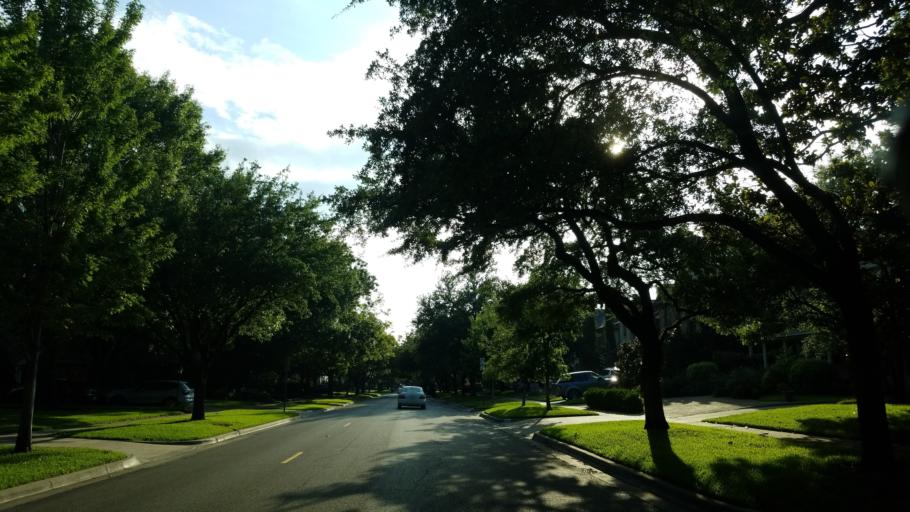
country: US
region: Texas
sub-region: Dallas County
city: University Park
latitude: 32.8451
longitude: -96.7911
